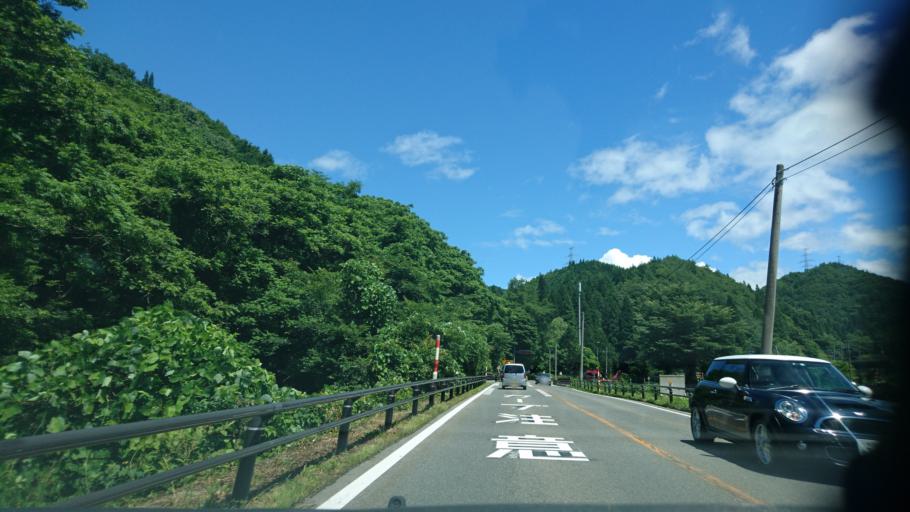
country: JP
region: Akita
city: Kakunodatemachi
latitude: 39.6585
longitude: 140.6720
